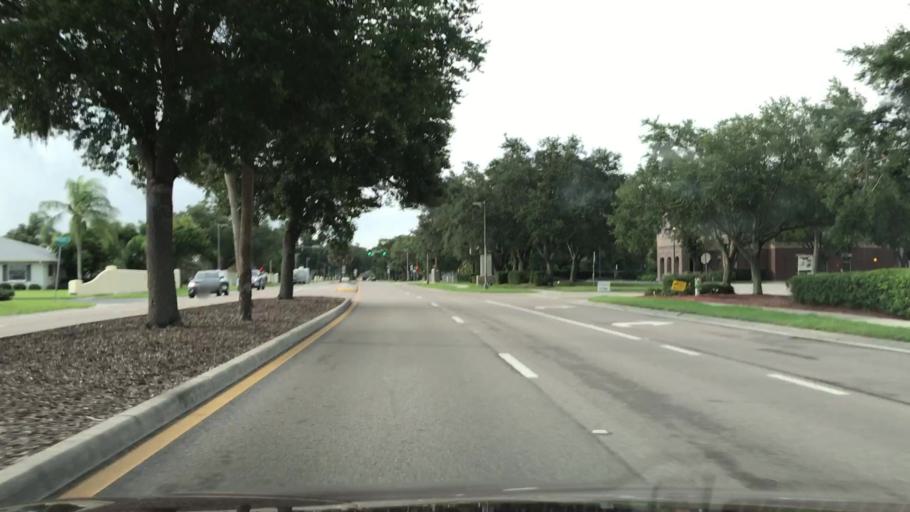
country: US
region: Florida
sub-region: Sarasota County
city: Plantation
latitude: 27.0710
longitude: -82.3889
